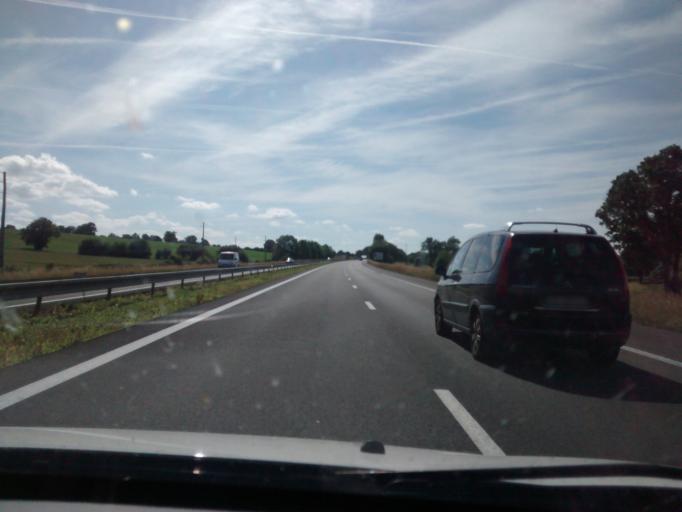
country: FR
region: Pays de la Loire
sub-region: Departement de la Mayenne
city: Vaiges
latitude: 48.0505
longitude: -0.4492
